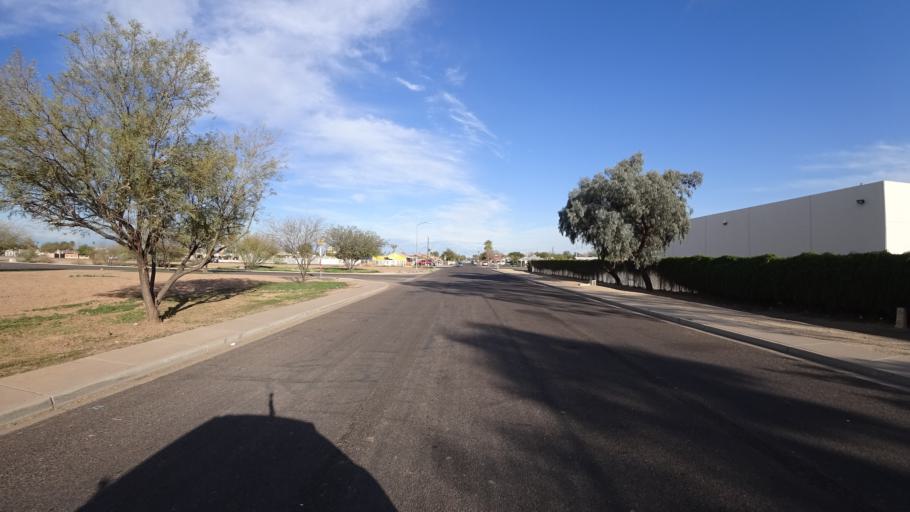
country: US
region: Arizona
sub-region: Maricopa County
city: Phoenix
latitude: 33.4550
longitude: -112.1402
